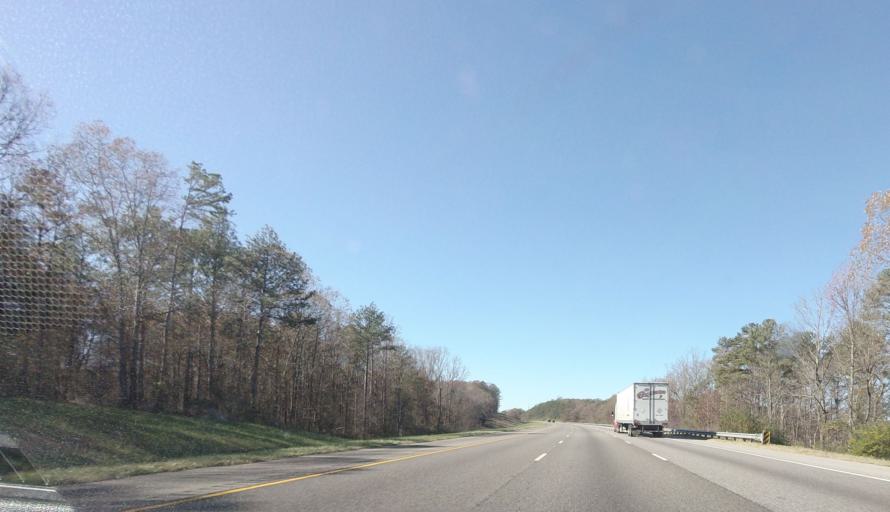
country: US
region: Alabama
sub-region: Calhoun County
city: Bynum
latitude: 33.5818
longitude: -85.9612
